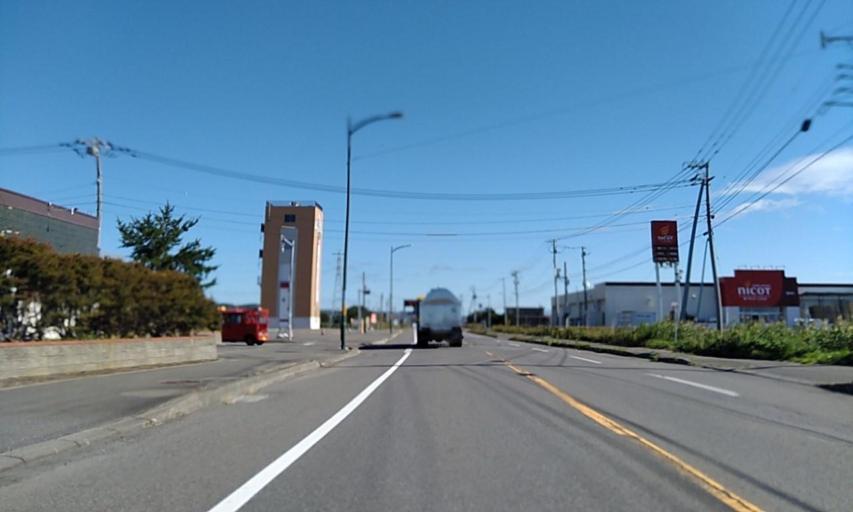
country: JP
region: Hokkaido
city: Shizunai-furukawacho
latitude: 42.5227
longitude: 142.0377
